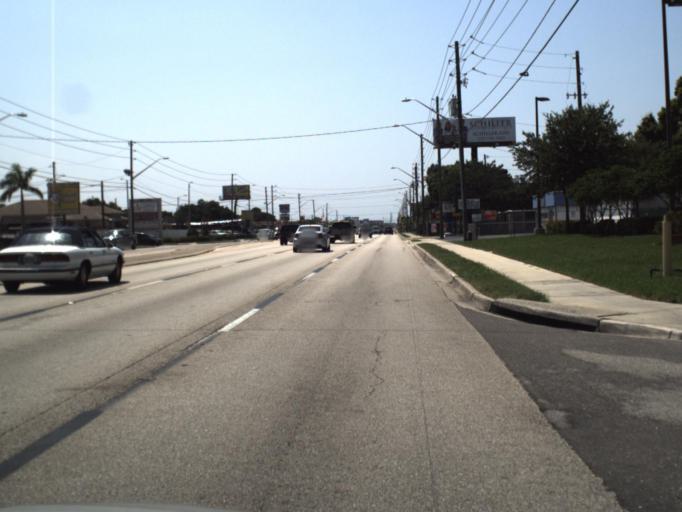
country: US
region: Florida
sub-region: Pinellas County
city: Kenneth City
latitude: 27.8393
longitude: -82.7408
